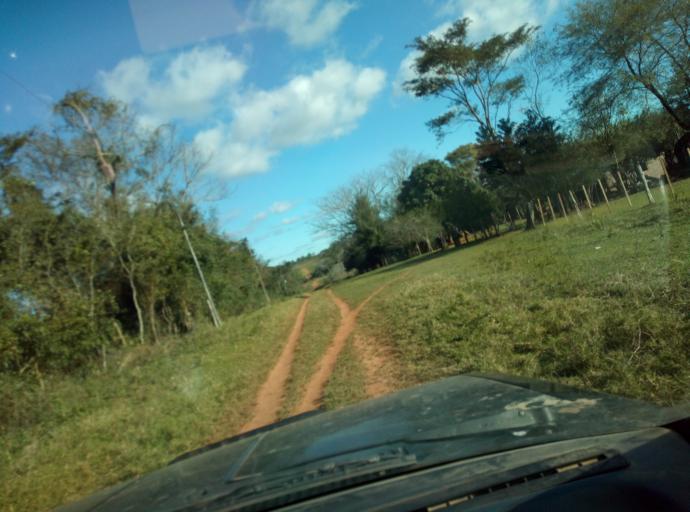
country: PY
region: Caaguazu
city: Doctor Cecilio Baez
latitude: -25.1695
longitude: -56.2729
